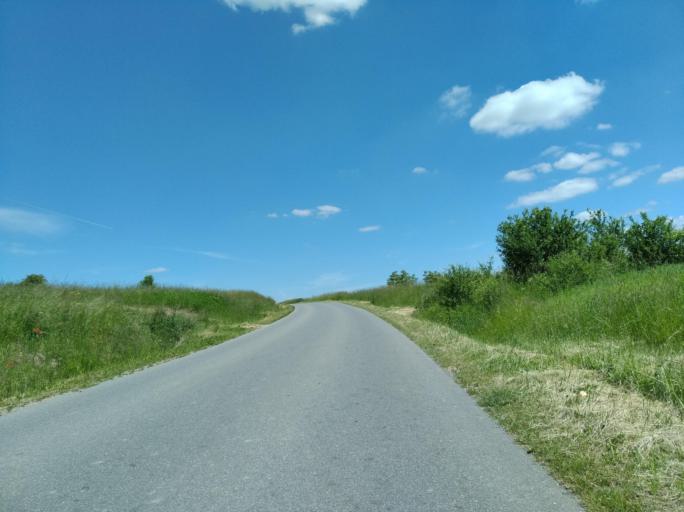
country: PL
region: Subcarpathian Voivodeship
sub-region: Powiat jasielski
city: Osiek Jasielski
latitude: 49.6534
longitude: 21.5295
